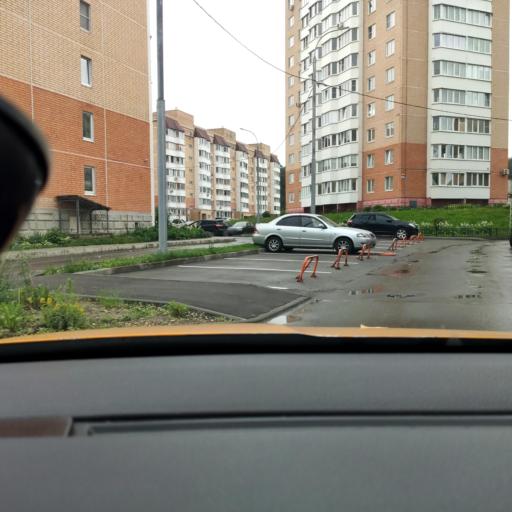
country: RU
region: Moskovskaya
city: Serpukhov
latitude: 54.9090
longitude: 37.3870
